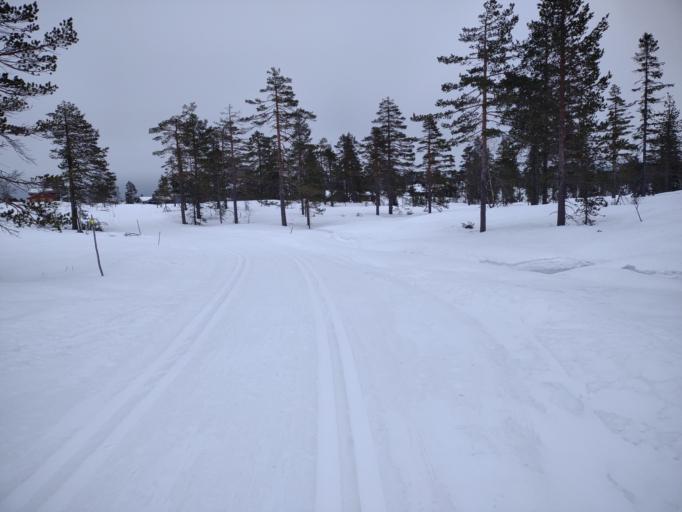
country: NO
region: Buskerud
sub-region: Flesberg
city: Lampeland
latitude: 59.7951
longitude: 9.4372
